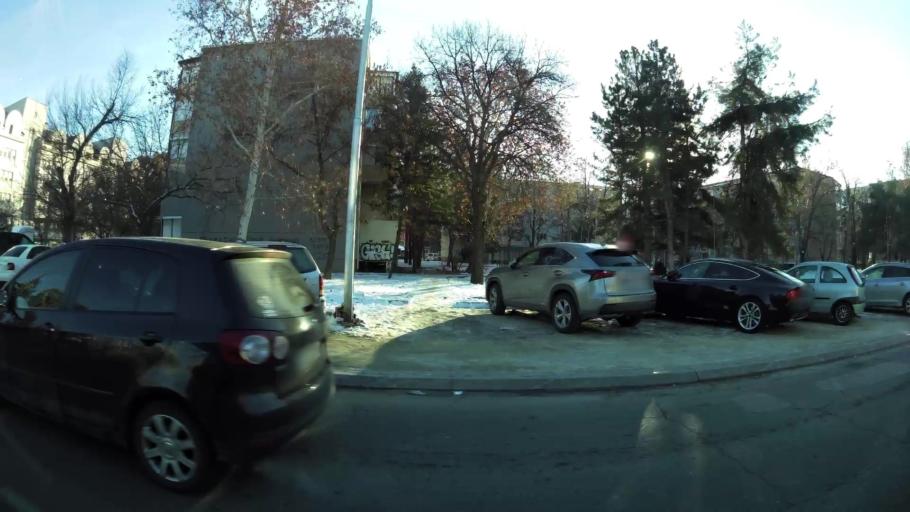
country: MK
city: Krushopek
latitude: 42.0074
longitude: 21.3838
